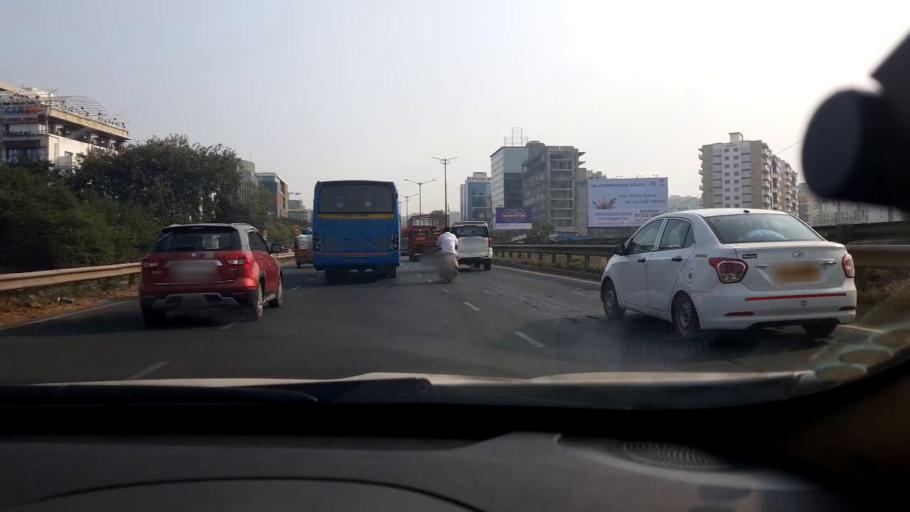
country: IN
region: Maharashtra
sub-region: Pune Division
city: Pimpri
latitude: 18.5566
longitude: 73.7704
